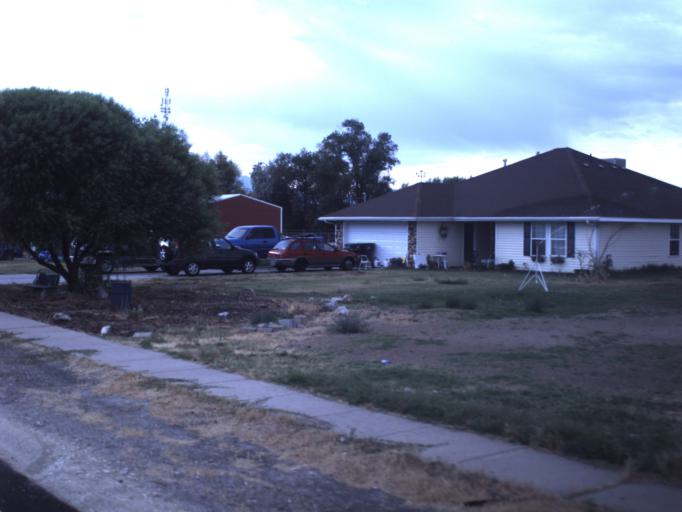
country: US
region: Utah
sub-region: Weber County
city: Hooper
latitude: 41.1639
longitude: -112.1184
